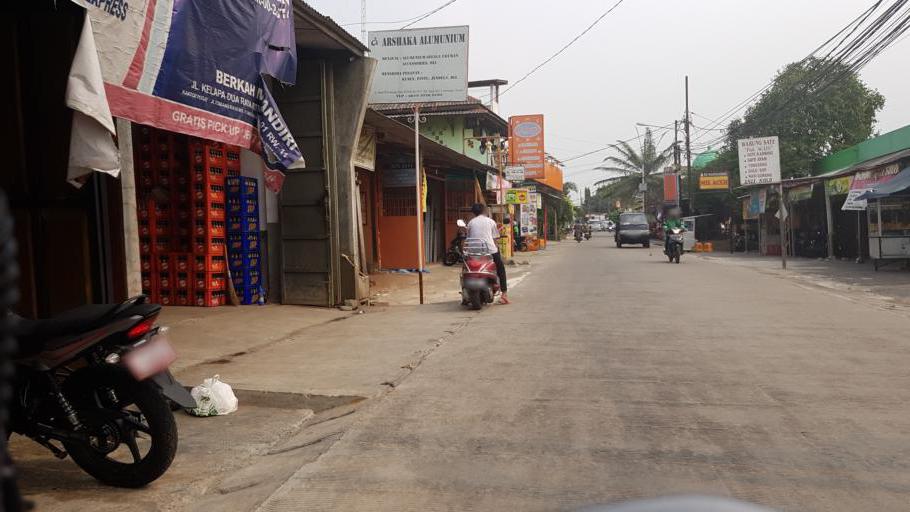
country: ID
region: West Java
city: Depok
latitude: -6.3640
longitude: 106.8431
